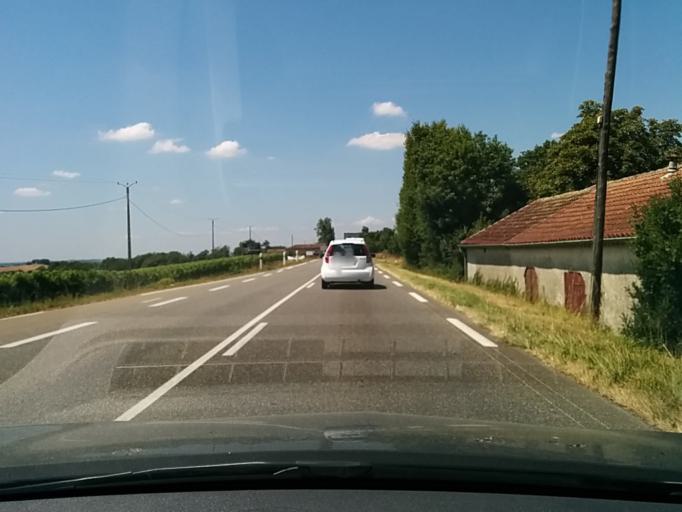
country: FR
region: Midi-Pyrenees
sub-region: Departement du Gers
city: Eauze
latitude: 43.7708
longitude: 0.1297
